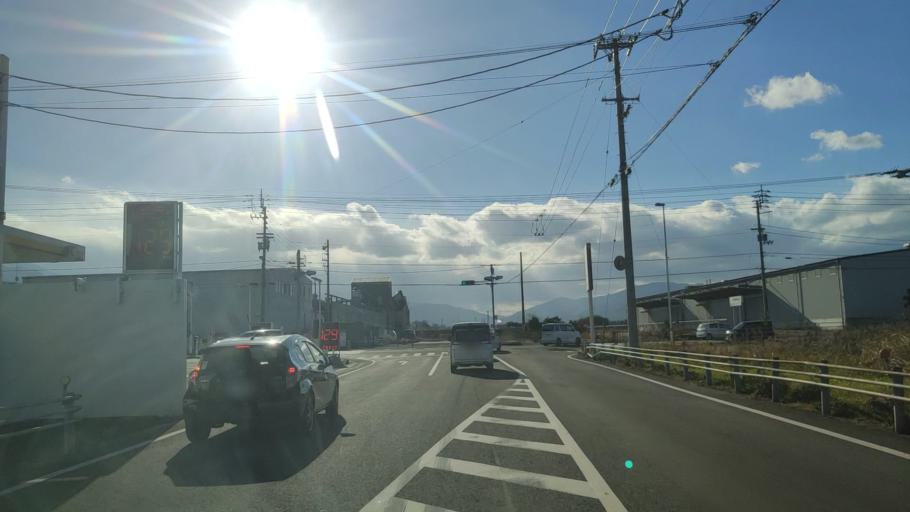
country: JP
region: Ehime
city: Saijo
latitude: 33.9107
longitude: 133.1117
